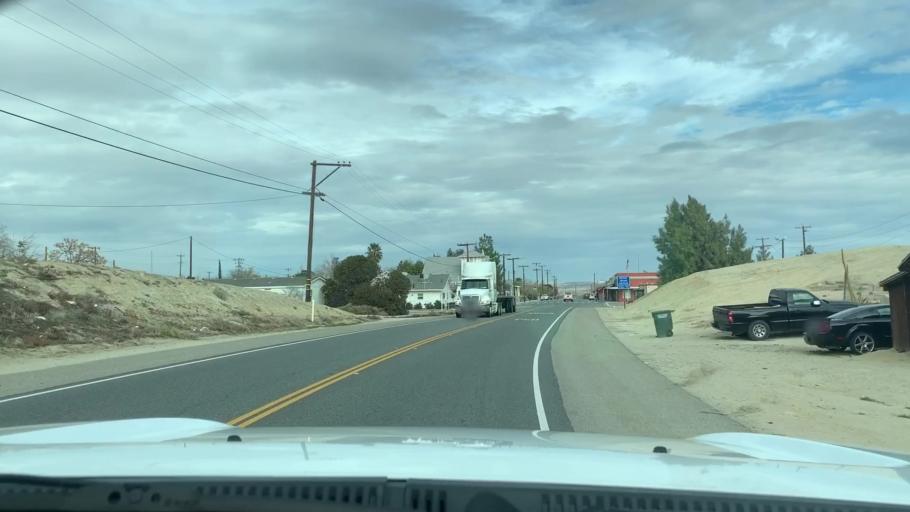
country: US
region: California
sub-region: Kern County
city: Maricopa
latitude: 35.0613
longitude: -119.4017
